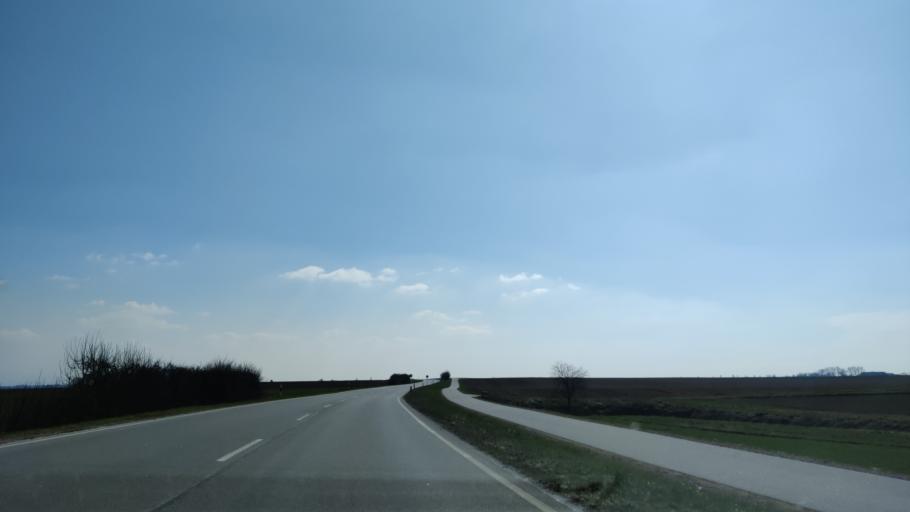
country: DE
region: Bavaria
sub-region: Lower Bavaria
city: Hunderdorf
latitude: 48.8418
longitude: 12.6721
